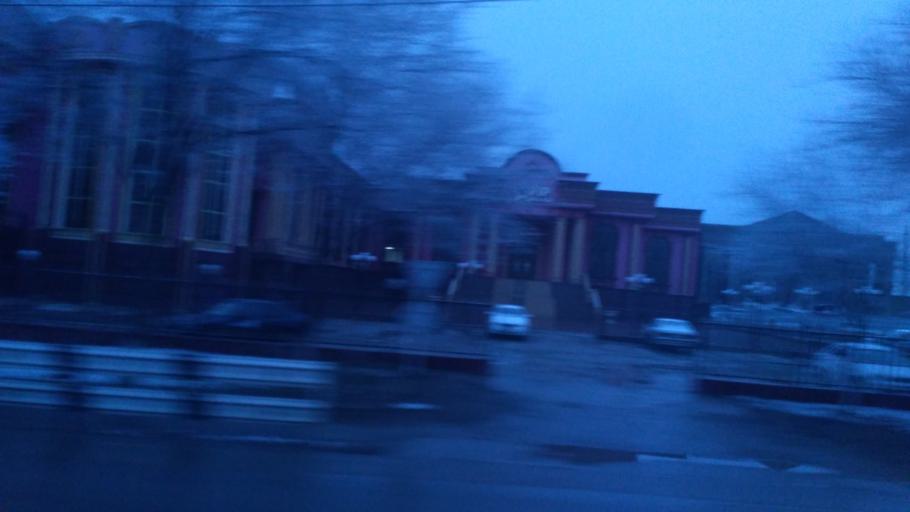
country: KZ
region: Ongtustik Qazaqstan
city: Shymkent
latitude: 42.3597
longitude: 69.5219
